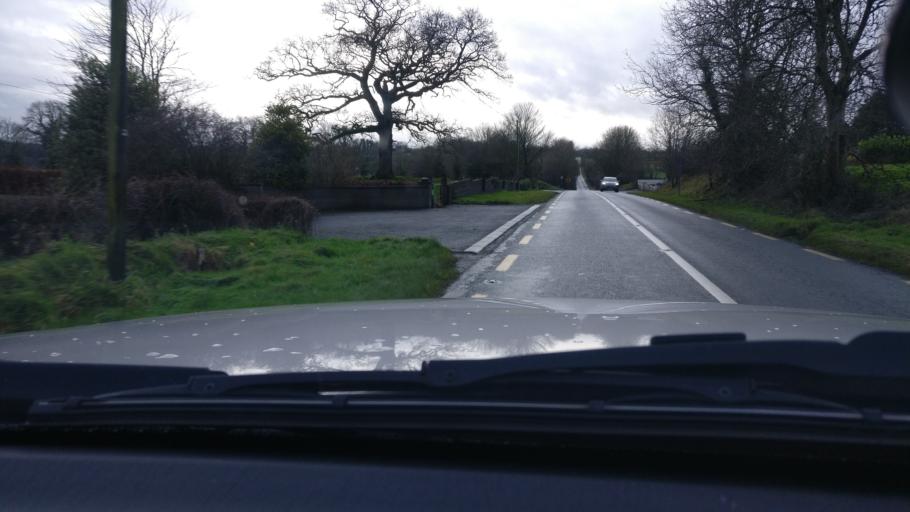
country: IE
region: Leinster
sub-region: An Iarmhi
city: Moate
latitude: 53.6246
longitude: -7.6970
